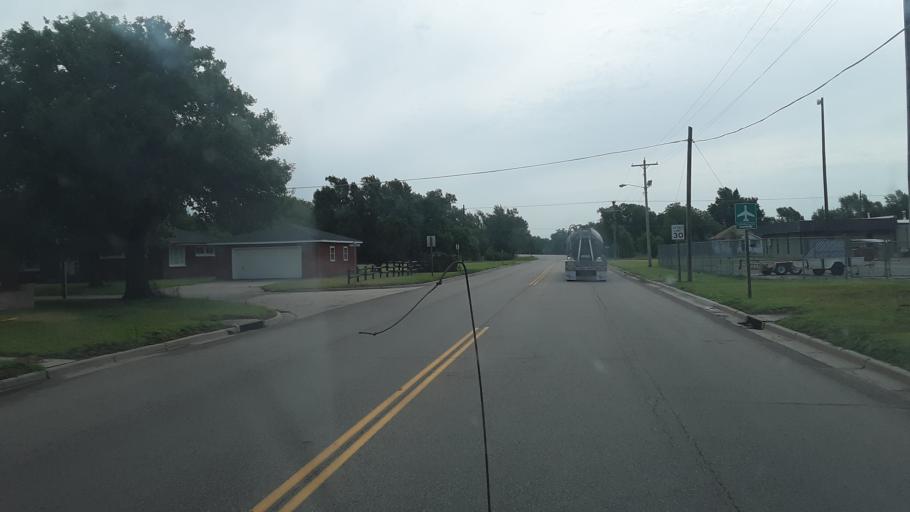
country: US
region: Kansas
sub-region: Edwards County
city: Kinsley
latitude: 37.9188
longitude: -99.4066
